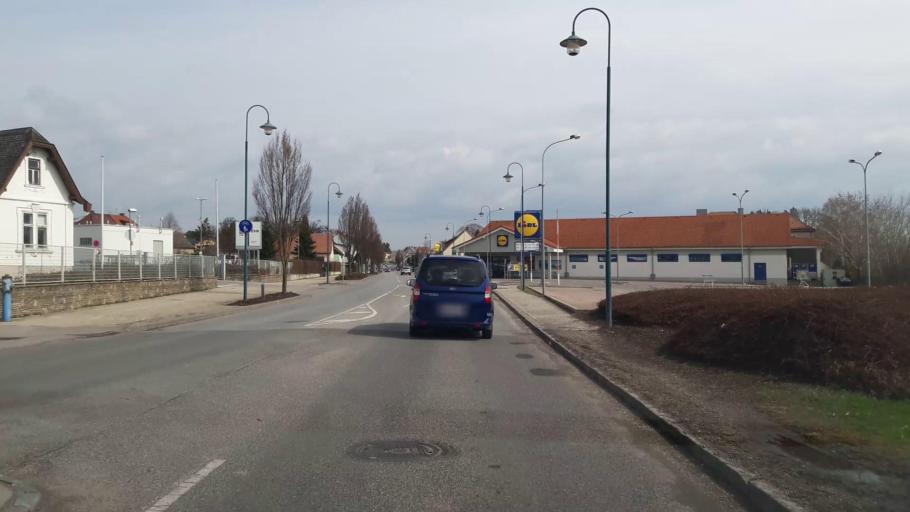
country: AT
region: Lower Austria
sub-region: Politischer Bezirk Mistelbach
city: Mistelbach
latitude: 48.5625
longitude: 16.5619
